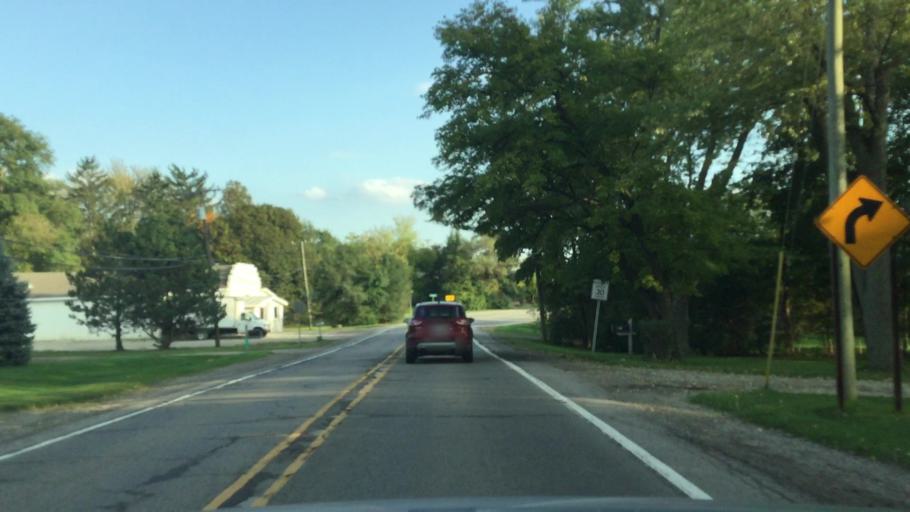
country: US
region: Michigan
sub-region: Oakland County
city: Wolverine Lake
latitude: 42.6192
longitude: -83.4482
